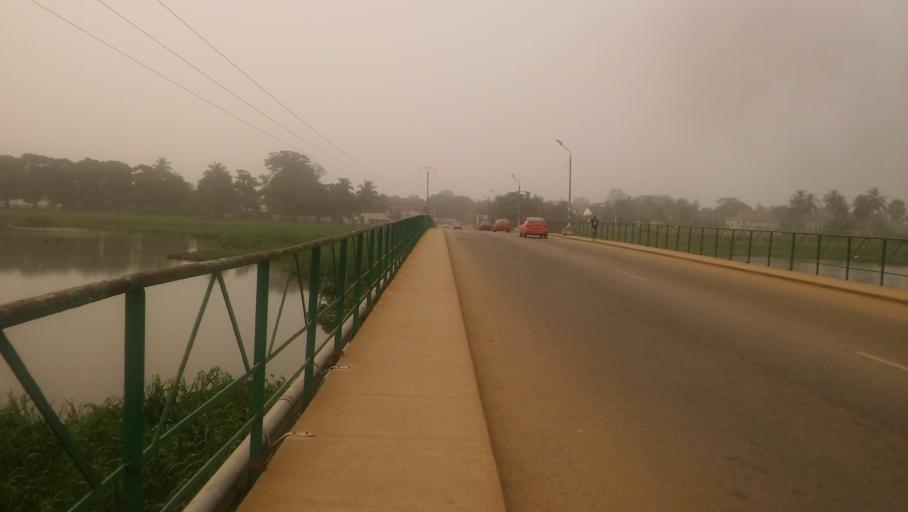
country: CI
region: Sud-Comoe
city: Grand-Bassam
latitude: 5.2002
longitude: -3.7368
